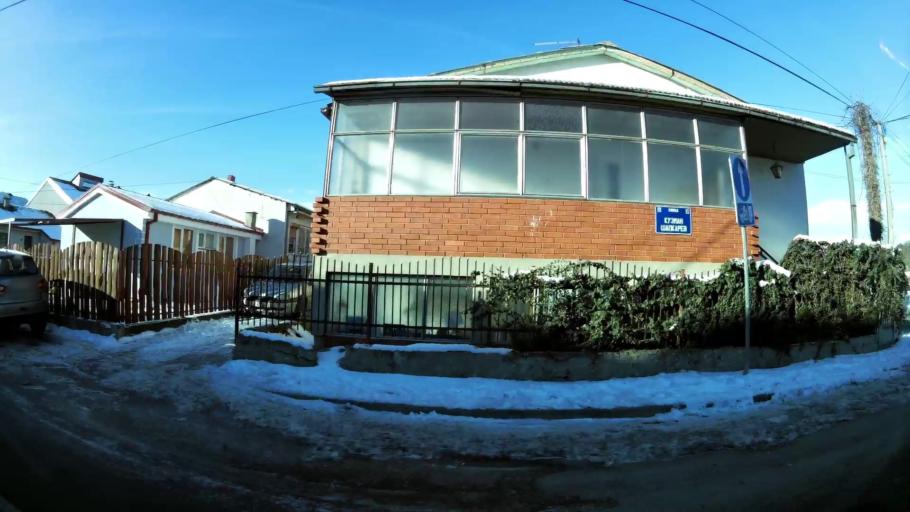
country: MK
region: Saraj
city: Saraj
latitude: 42.0101
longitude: 21.3397
